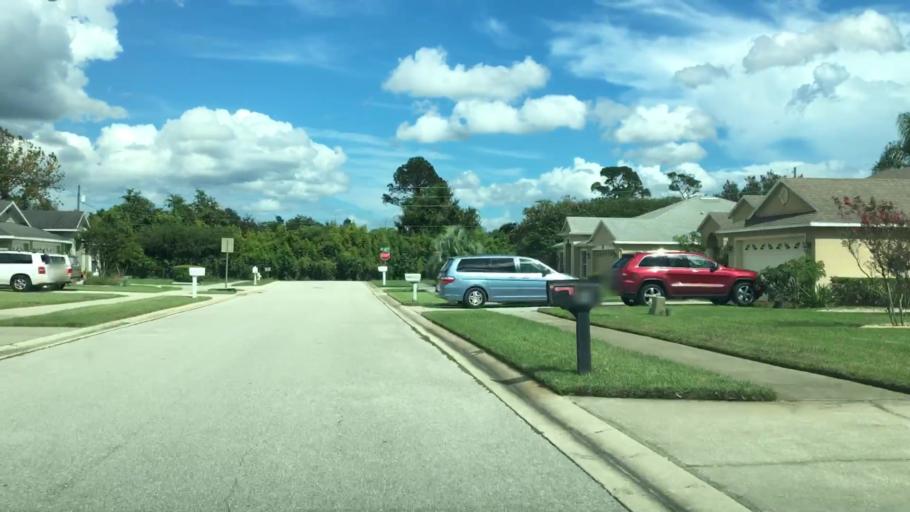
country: US
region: Florida
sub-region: Volusia County
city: Deltona
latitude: 28.8699
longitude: -81.2339
